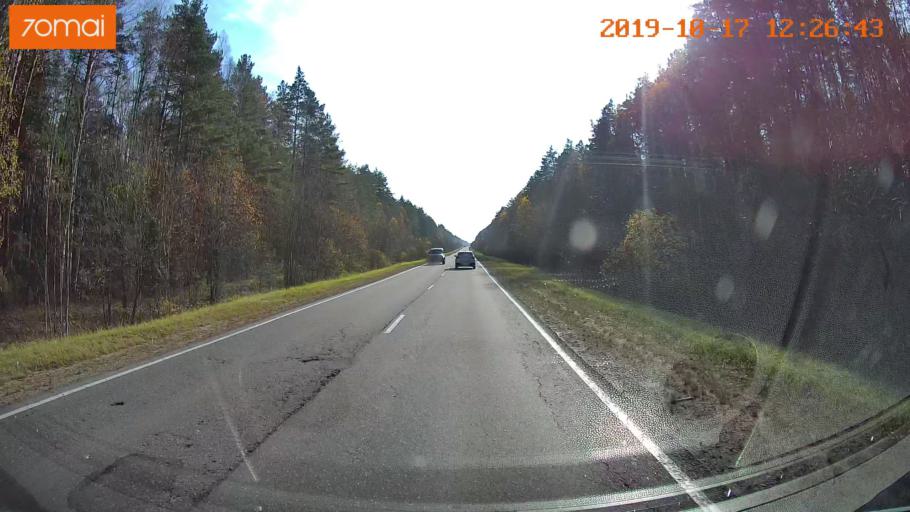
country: RU
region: Rjazan
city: Syntul
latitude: 55.0154
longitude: 41.2580
